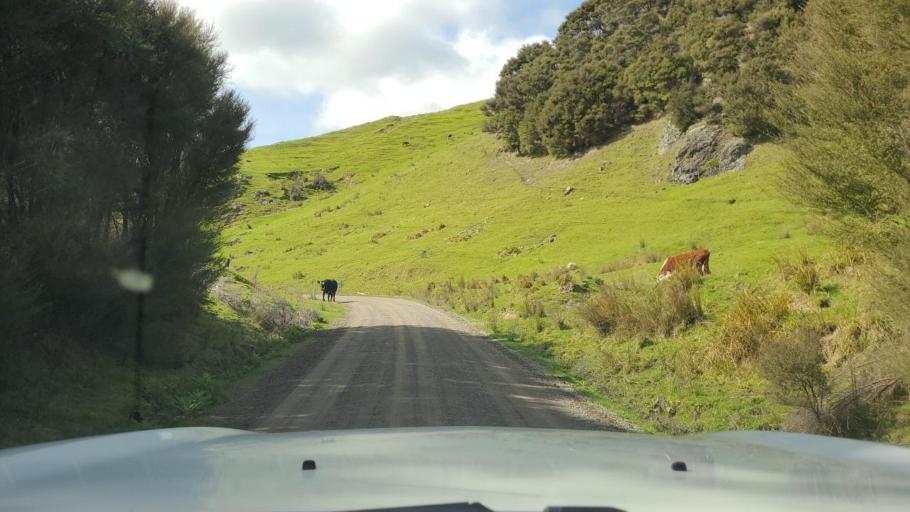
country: NZ
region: Wellington
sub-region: South Wairarapa District
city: Waipawa
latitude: -41.3605
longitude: 175.6996
